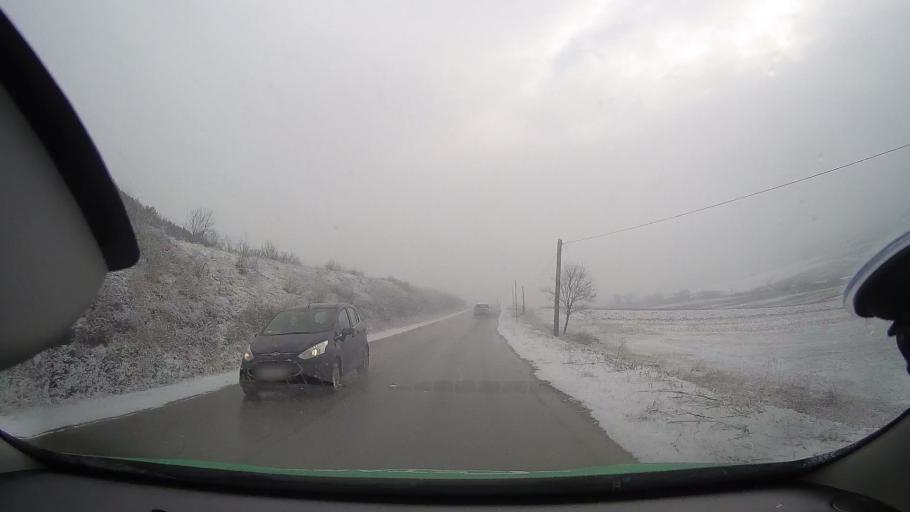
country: RO
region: Alba
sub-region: Comuna Lopadea Noua
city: Lopadea Noua
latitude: 46.3017
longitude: 23.8057
